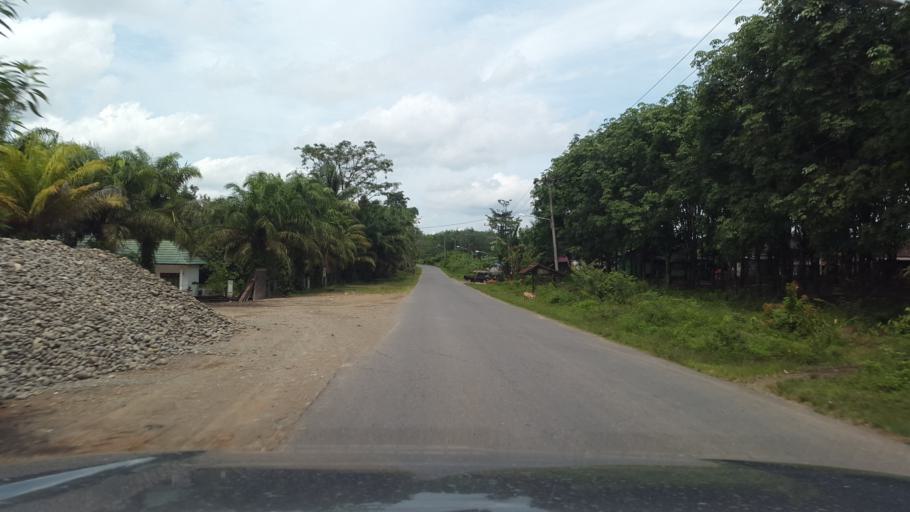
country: ID
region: South Sumatra
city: Gunungmegang Dalam
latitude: -3.3694
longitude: 103.9425
